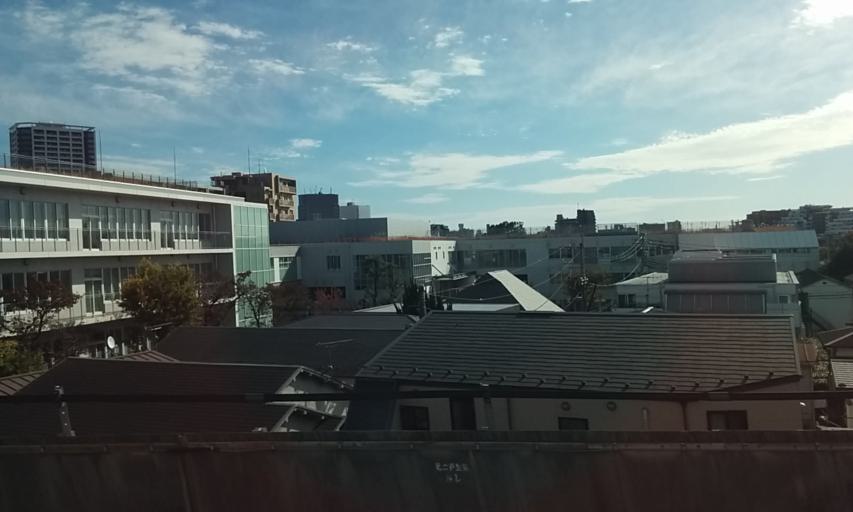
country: JP
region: Kanagawa
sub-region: Kawasaki-shi
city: Kawasaki
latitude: 35.6076
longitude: 139.7245
